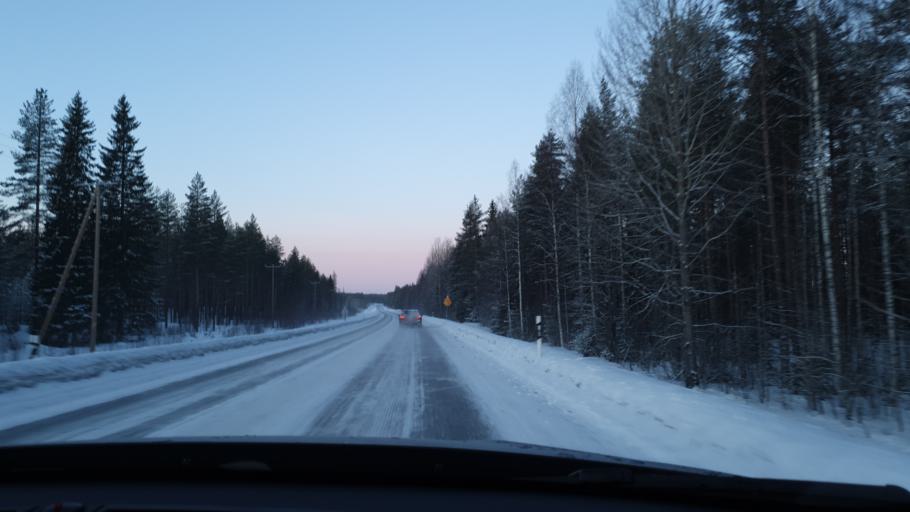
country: FI
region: Kainuu
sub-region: Kajaani
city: Sotkamo
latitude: 64.0872
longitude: 28.5879
